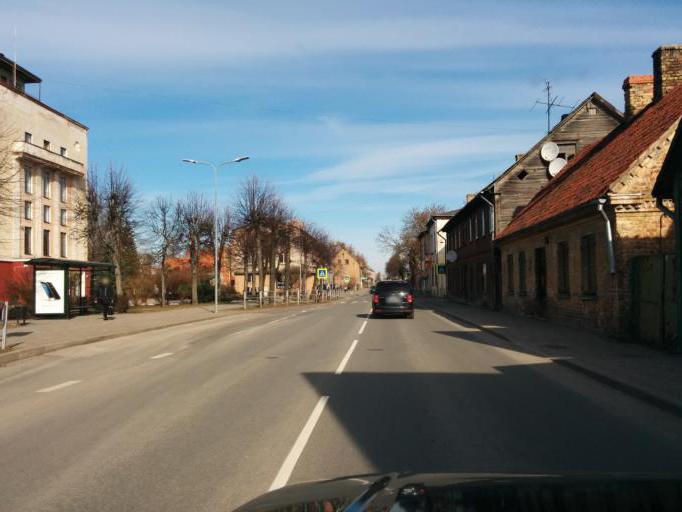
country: LV
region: Jelgava
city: Jelgava
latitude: 56.6440
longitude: 23.7232
